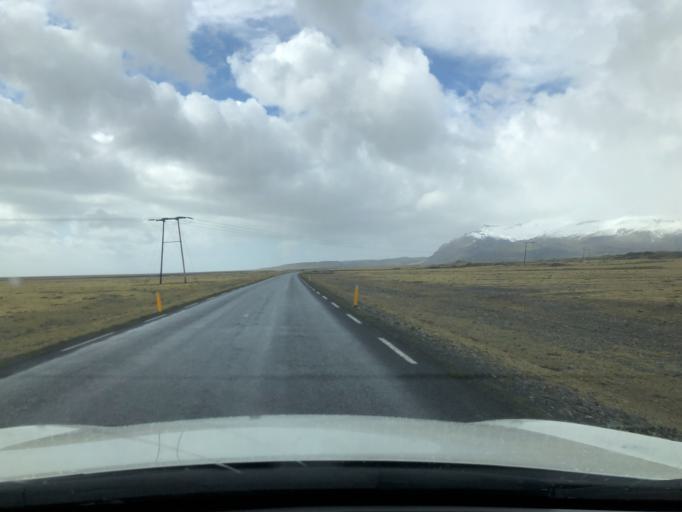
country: IS
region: East
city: Hoefn
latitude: 64.0117
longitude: -16.3576
